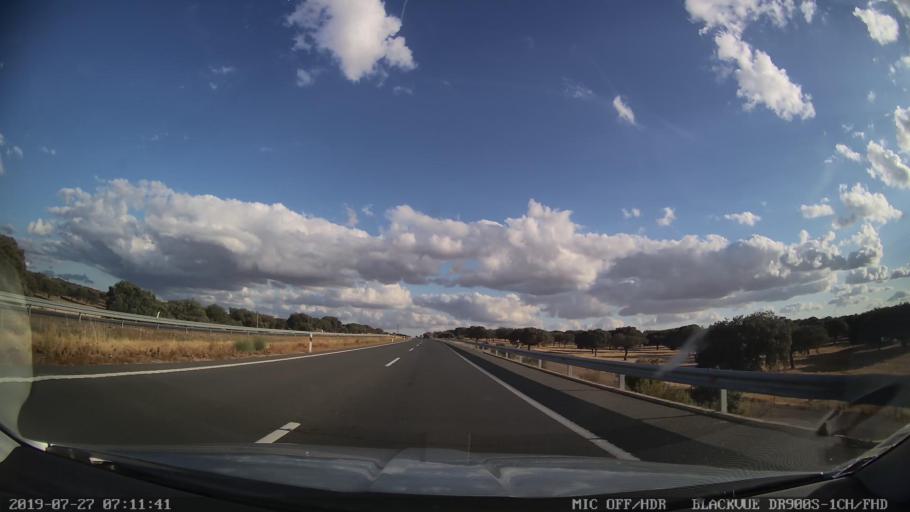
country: ES
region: Extremadura
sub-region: Provincia de Caceres
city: Torrecillas de la Tiesa
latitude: 39.5478
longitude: -5.8335
